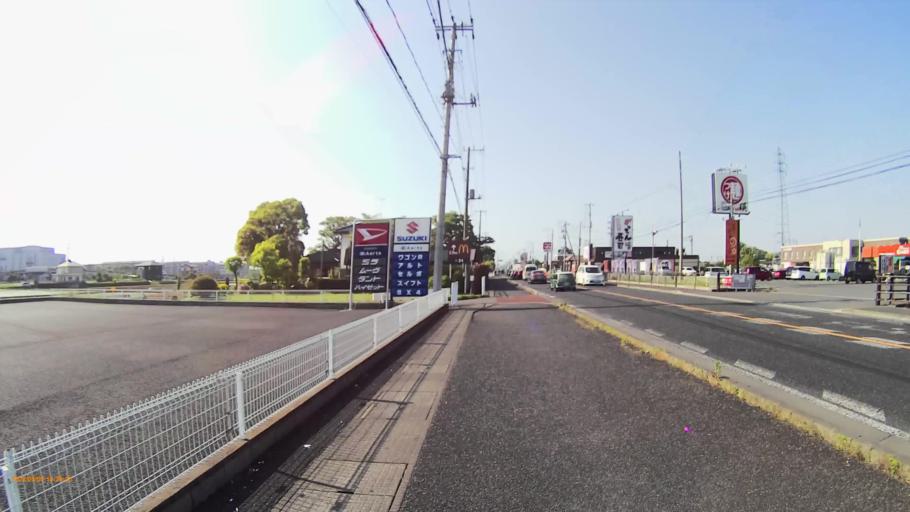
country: JP
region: Saitama
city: Sugito
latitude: 36.0448
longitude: 139.7195
